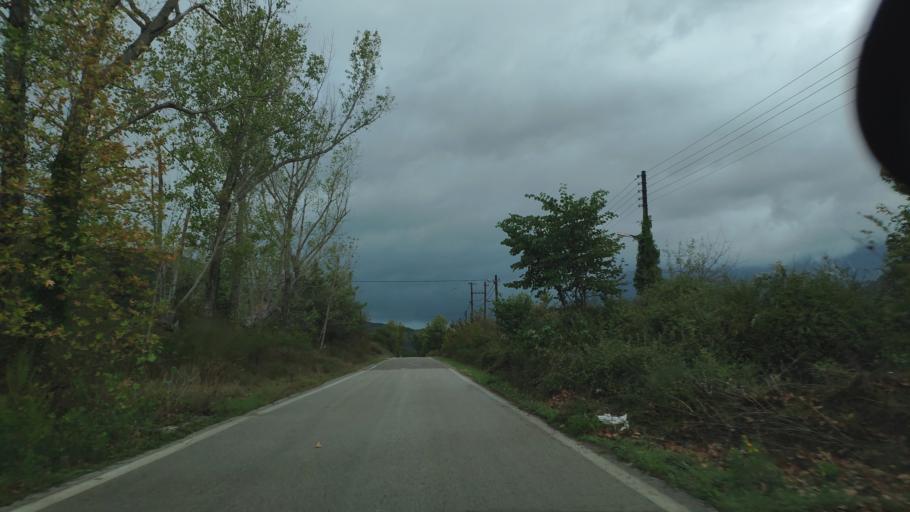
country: GR
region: West Greece
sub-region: Nomos Aitolias kai Akarnanias
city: Krikellos
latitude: 38.9899
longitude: 21.3157
